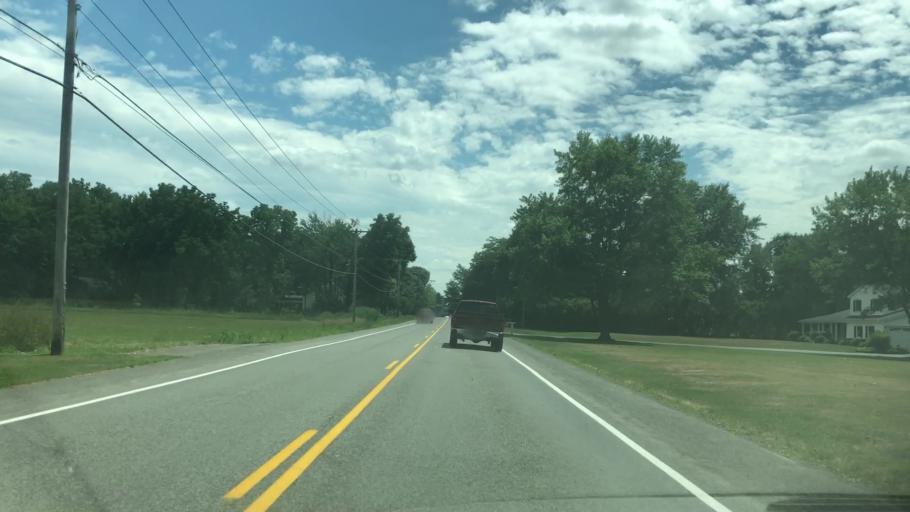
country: US
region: New York
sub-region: Monroe County
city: Fairport
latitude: 43.1413
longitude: -77.4006
